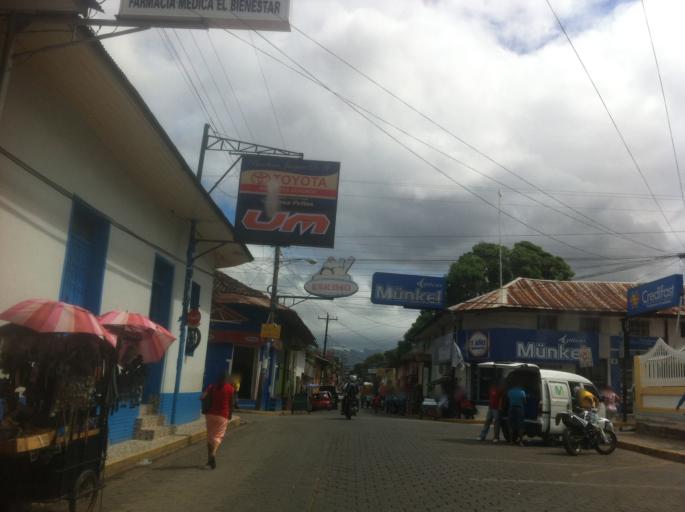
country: NI
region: Chontales
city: Juigalpa
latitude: 12.1068
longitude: -85.3646
